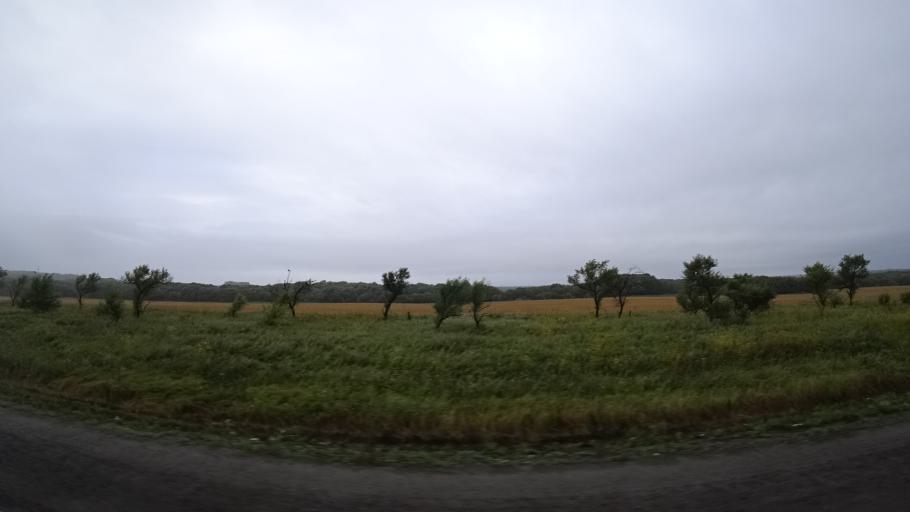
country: RU
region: Primorskiy
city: Monastyrishche
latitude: 44.2800
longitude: 132.4911
